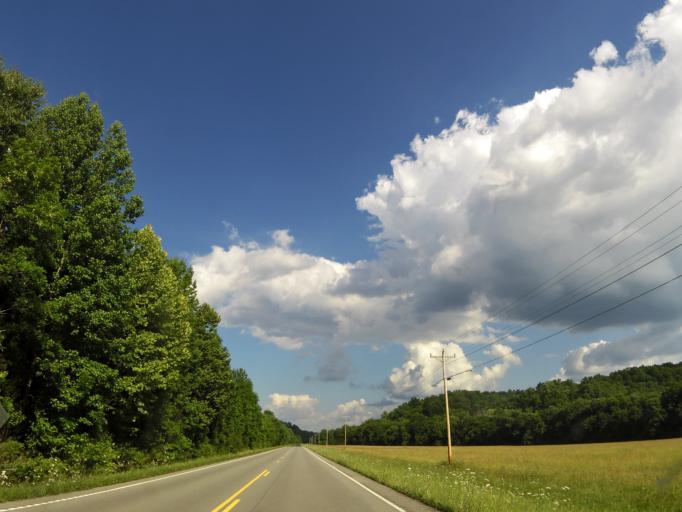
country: US
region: Tennessee
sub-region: Perry County
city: Linden
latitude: 35.6155
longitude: -87.7281
